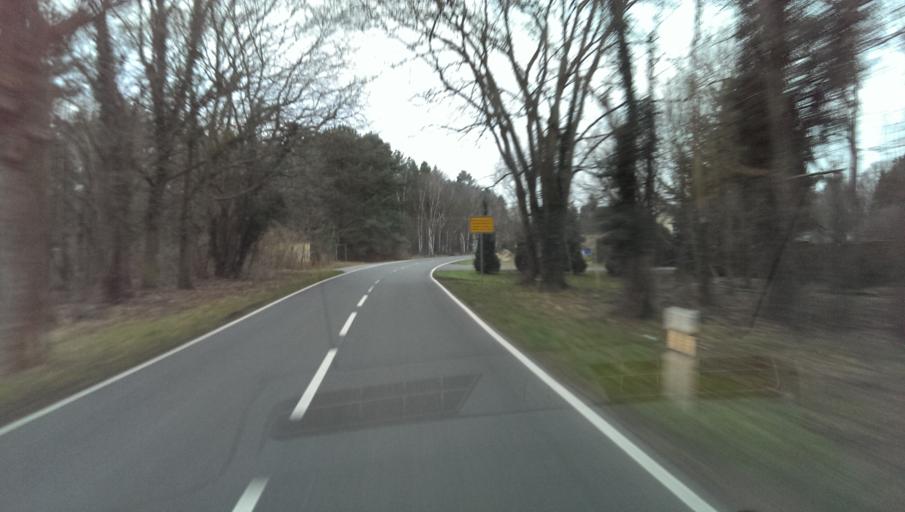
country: DE
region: Brandenburg
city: Sperenberg
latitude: 52.1553
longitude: 13.3507
